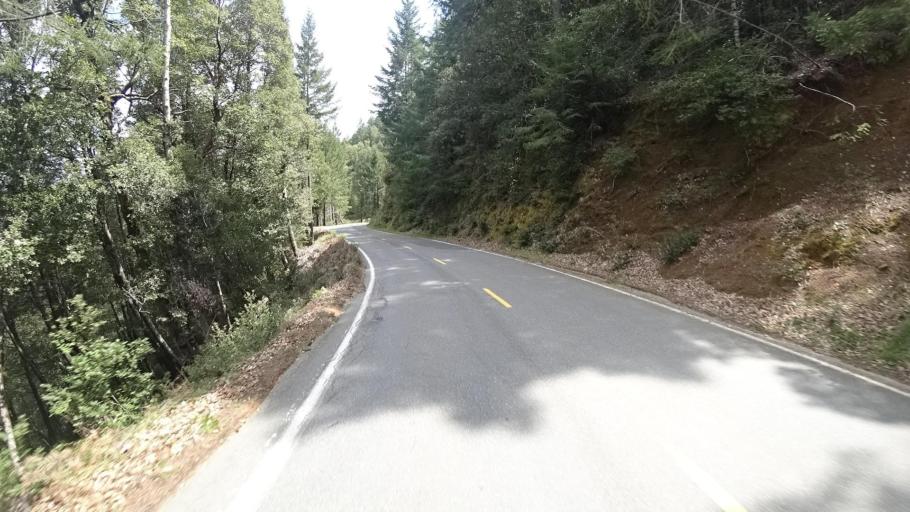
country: US
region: California
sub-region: Humboldt County
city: Redway
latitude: 40.0542
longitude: -123.9885
